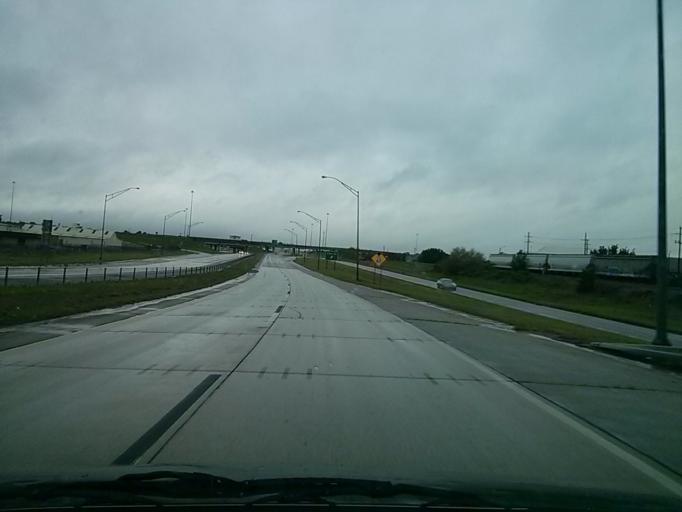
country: US
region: Oklahoma
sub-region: Tulsa County
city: Oakhurst
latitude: 36.0931
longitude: -96.0360
